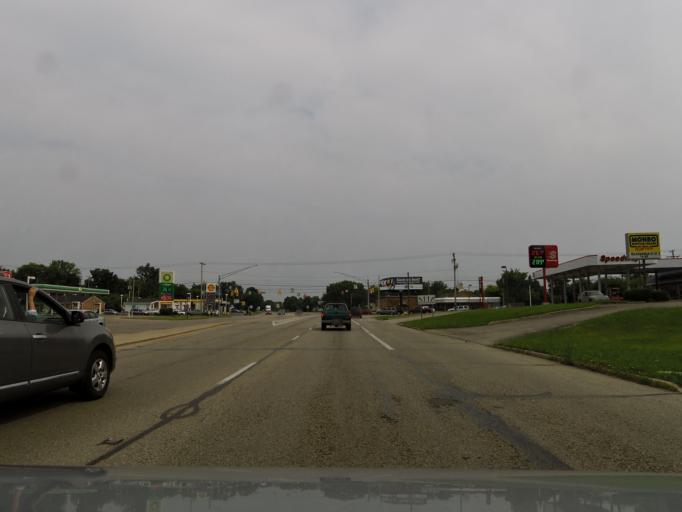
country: US
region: Ohio
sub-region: Montgomery County
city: Riverside
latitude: 39.7584
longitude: -84.1202
